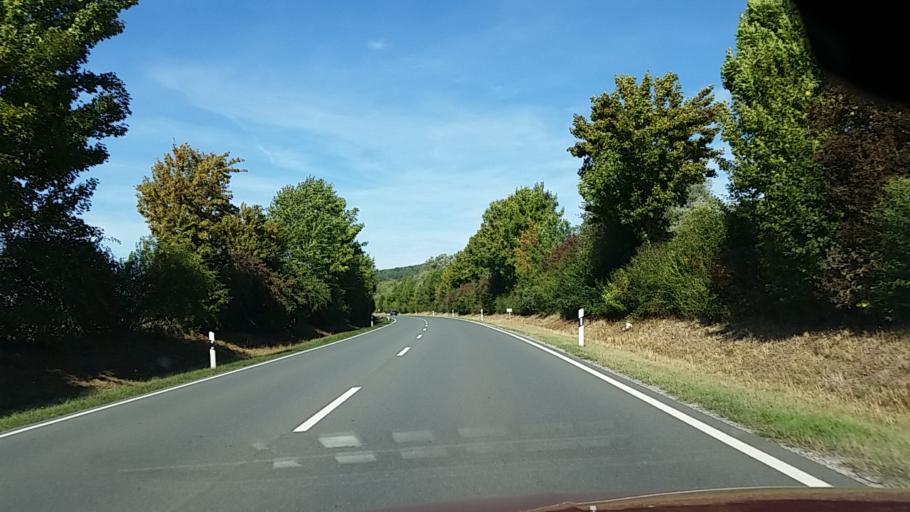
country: DE
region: Bavaria
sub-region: Regierungsbezirk Unterfranken
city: Zellingen
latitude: 49.9141
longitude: 9.8174
